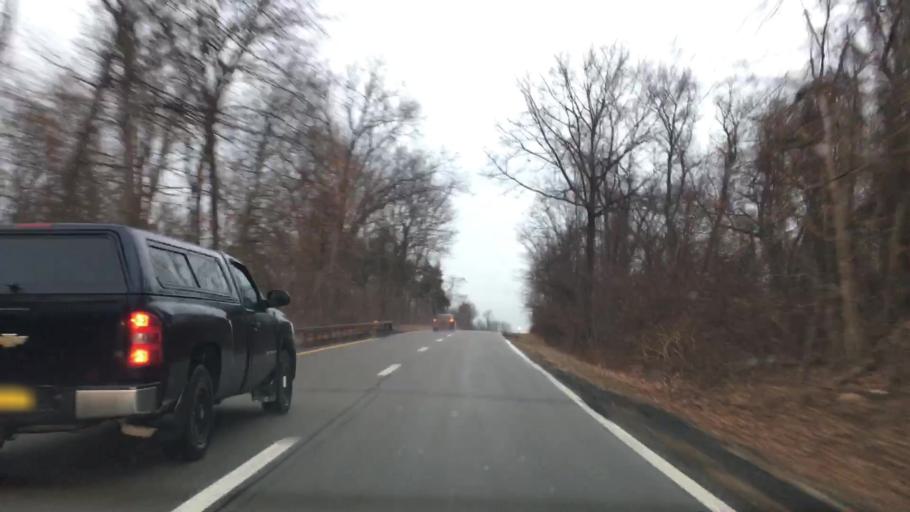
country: US
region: New York
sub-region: Dutchess County
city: Hillside Lake
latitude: 41.5665
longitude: -73.7818
